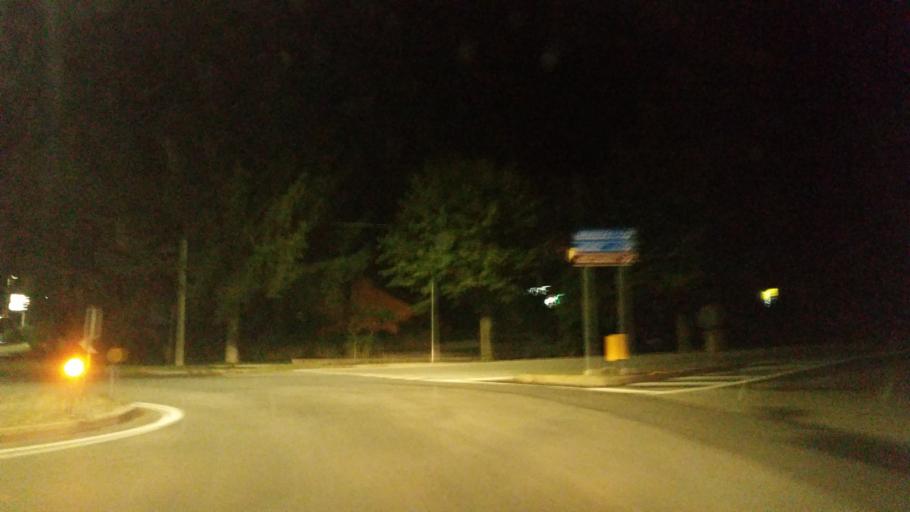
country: IT
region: Piedmont
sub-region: Provincia di Cuneo
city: Camerana
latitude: 44.4453
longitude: 8.1424
